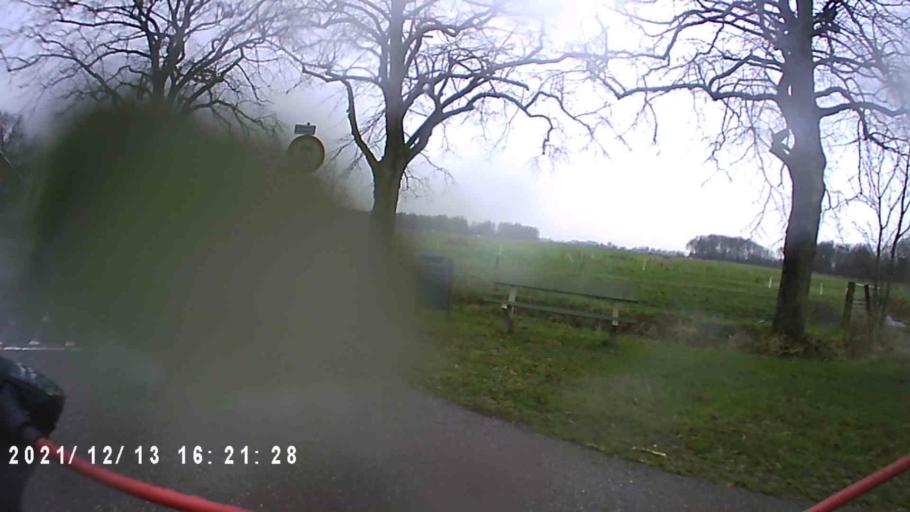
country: NL
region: Groningen
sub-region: Gemeente Delfzijl
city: Delfzijl
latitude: 53.3356
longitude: 6.8963
